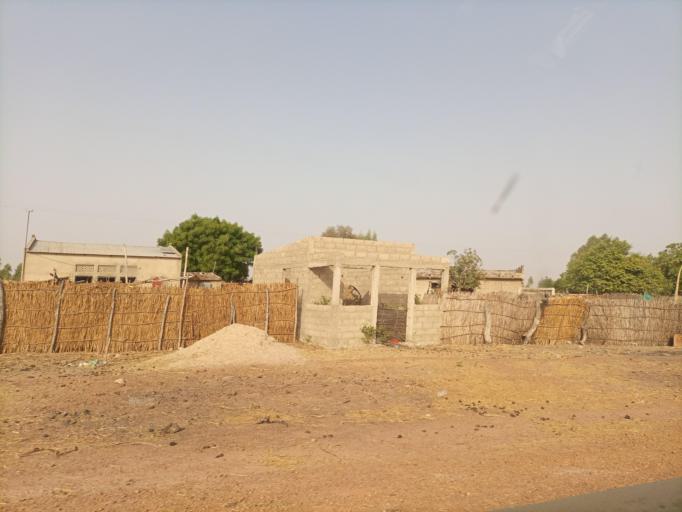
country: SN
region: Fatick
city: Passi
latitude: 14.0400
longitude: -16.3204
